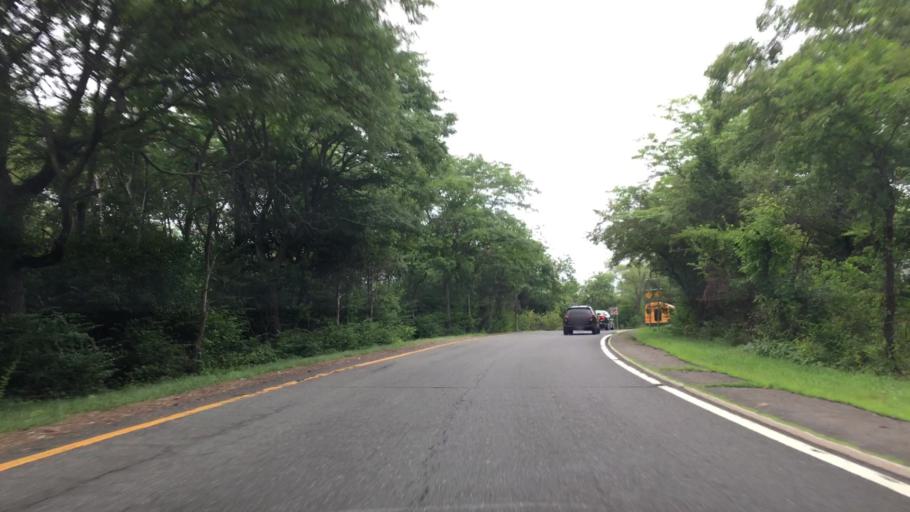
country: US
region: New York
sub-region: Nassau County
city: Syosset
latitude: 40.8097
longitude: -73.4910
